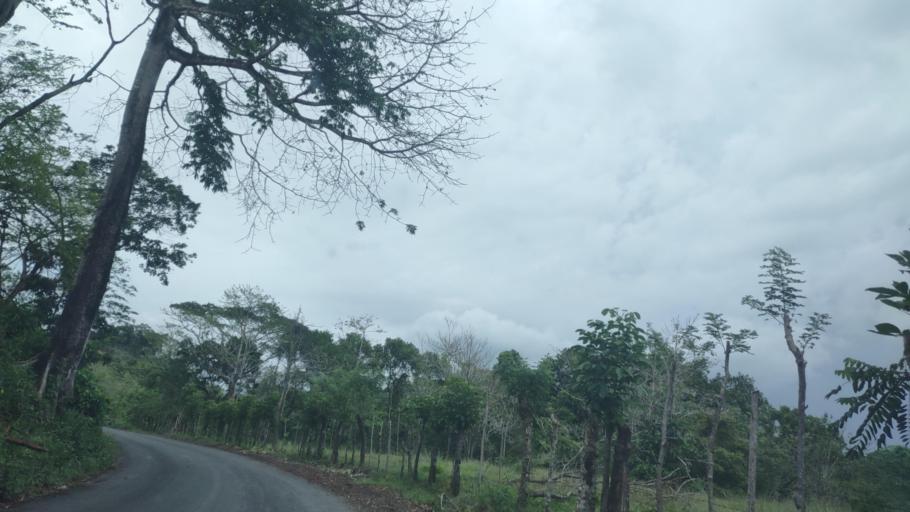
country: MX
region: Tabasco
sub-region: Huimanguillo
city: Francisco Rueda
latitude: 17.5244
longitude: -94.1287
